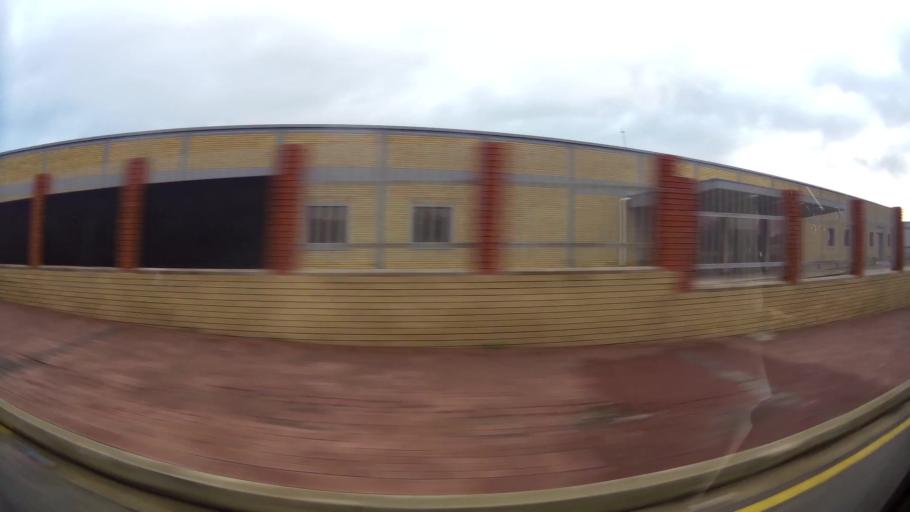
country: ZA
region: Eastern Cape
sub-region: Nelson Mandela Bay Metropolitan Municipality
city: Port Elizabeth
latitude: -33.9246
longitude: 25.5964
